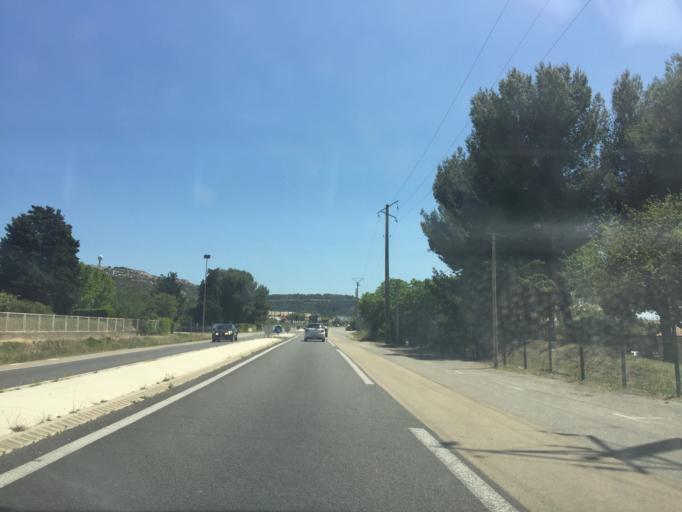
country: FR
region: Provence-Alpes-Cote d'Azur
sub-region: Departement des Bouches-du-Rhone
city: Rognac
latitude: 43.4807
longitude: 5.2259
